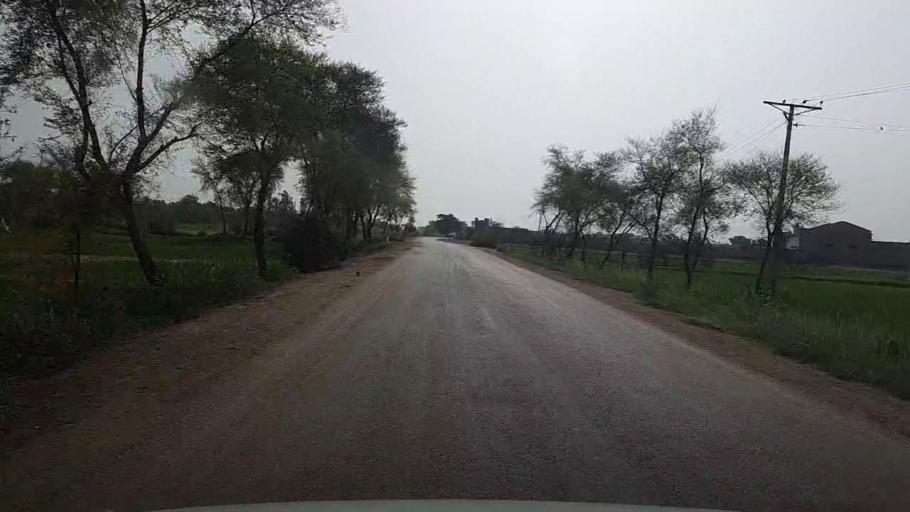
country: PK
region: Sindh
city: Mehar
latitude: 27.1208
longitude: 67.8135
